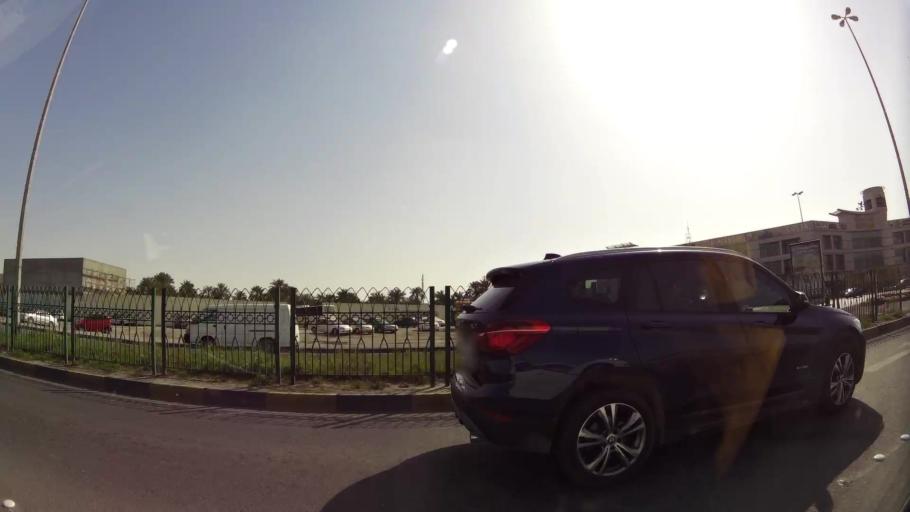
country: BH
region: Manama
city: Jidd Hafs
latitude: 26.2198
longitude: 50.5114
